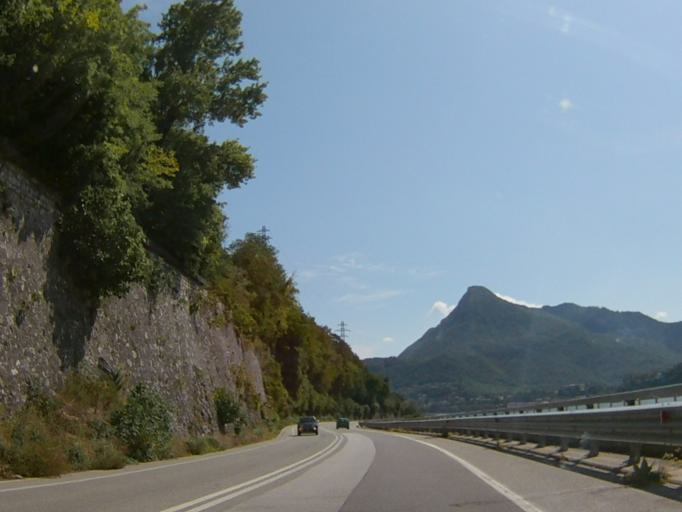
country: IT
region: Lombardy
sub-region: Provincia di Lecco
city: Lecco
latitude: 45.8723
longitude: 9.3776
